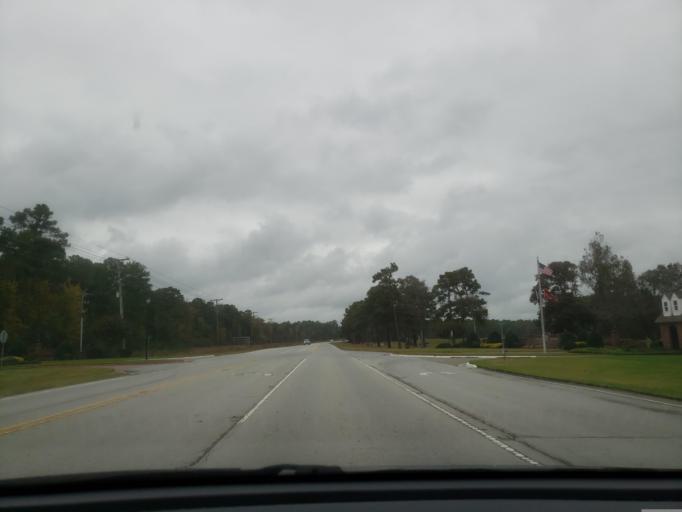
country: US
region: North Carolina
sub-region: Onslow County
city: Sneads Ferry
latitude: 34.5094
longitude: -77.4337
